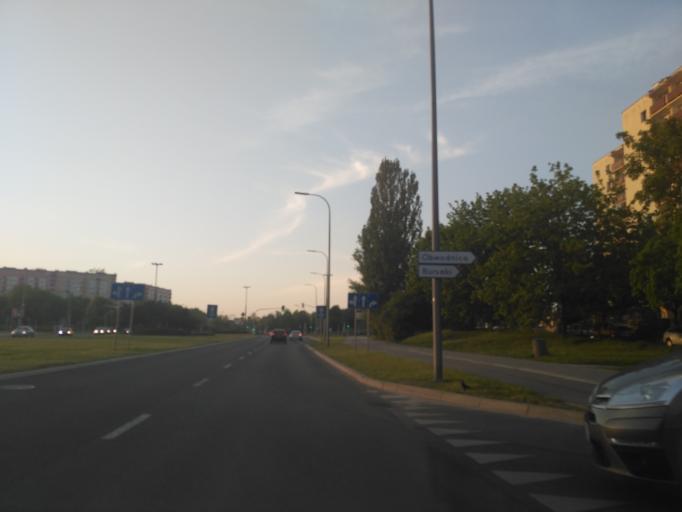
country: PL
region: Lublin Voivodeship
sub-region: Powiat lubelski
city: Lublin
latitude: 51.2610
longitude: 22.5526
